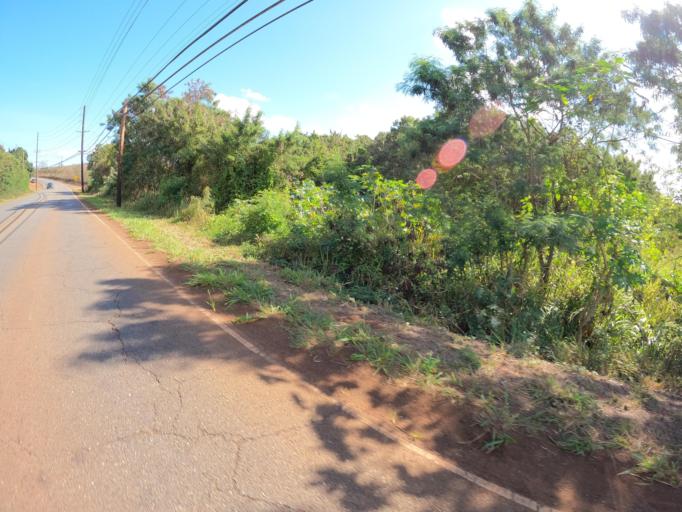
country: US
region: Hawaii
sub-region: Honolulu County
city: Hale'iwa
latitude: 21.5658
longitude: -158.1105
